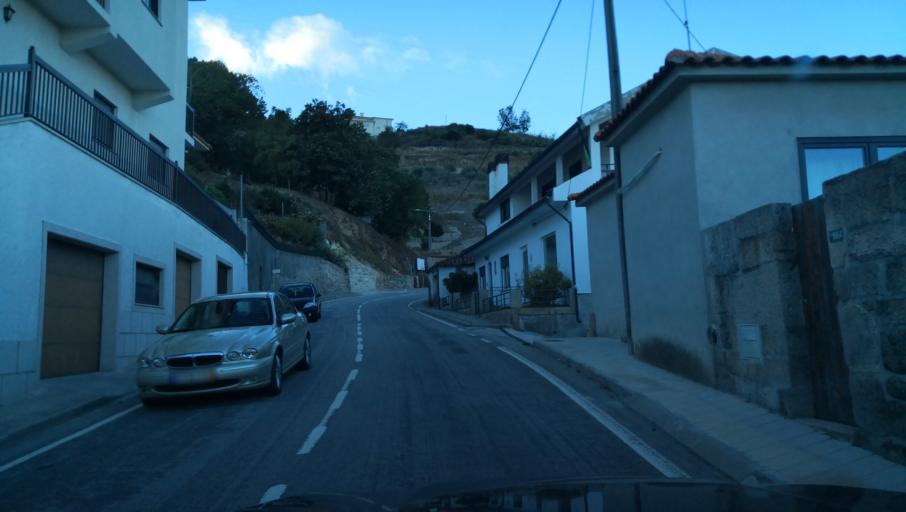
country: PT
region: Vila Real
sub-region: Santa Marta de Penaguiao
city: Santa Marta de Penaguiao
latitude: 41.2533
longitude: -7.7721
